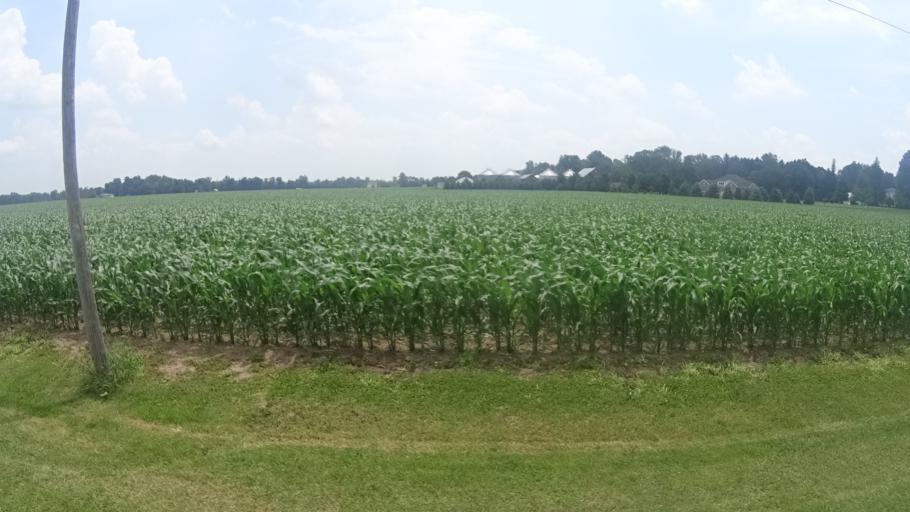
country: US
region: Ohio
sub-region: Erie County
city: Milan
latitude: 41.3075
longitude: -82.6313
